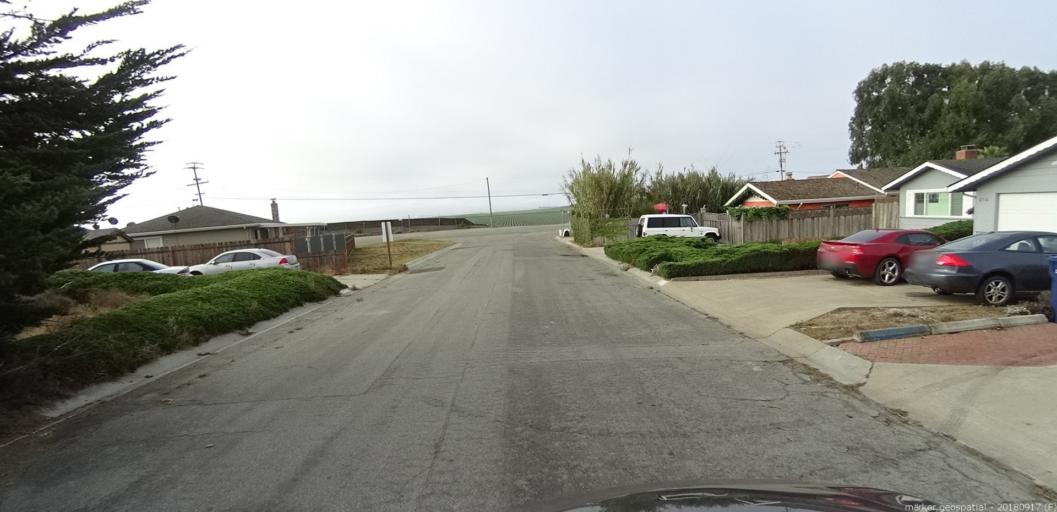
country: US
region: California
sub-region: Monterey County
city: Castroville
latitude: 36.7908
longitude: -121.7880
